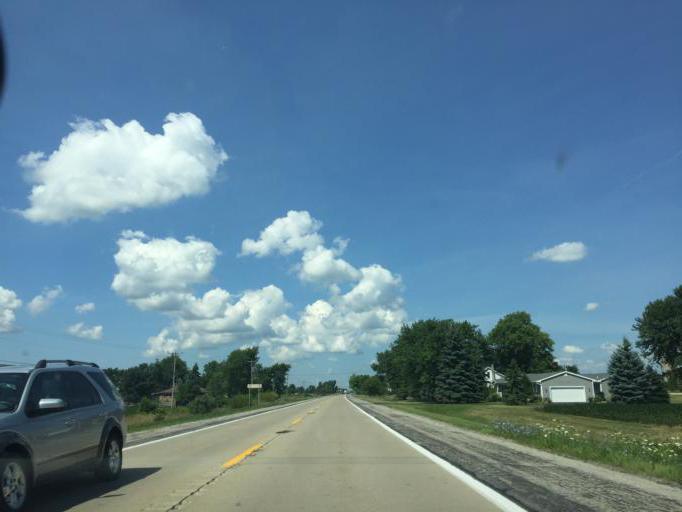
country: US
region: Ohio
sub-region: Lucas County
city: Sylvania
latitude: 41.7968
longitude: -83.7178
